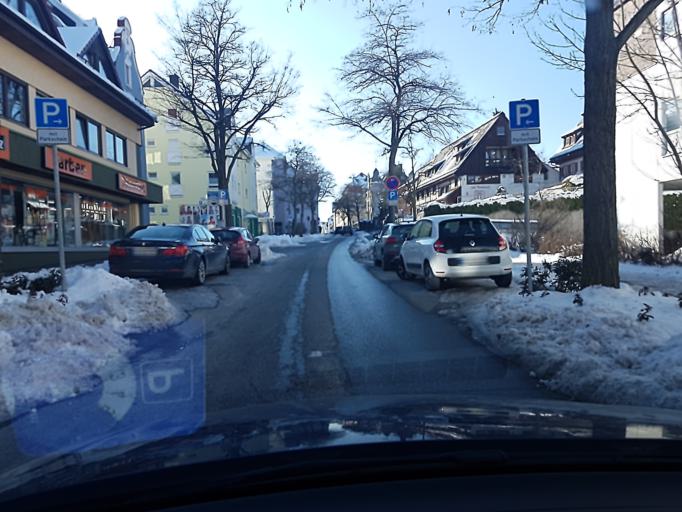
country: DE
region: Baden-Wuerttemberg
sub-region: Freiburg Region
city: Dauchingen
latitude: 48.0632
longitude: 8.5326
